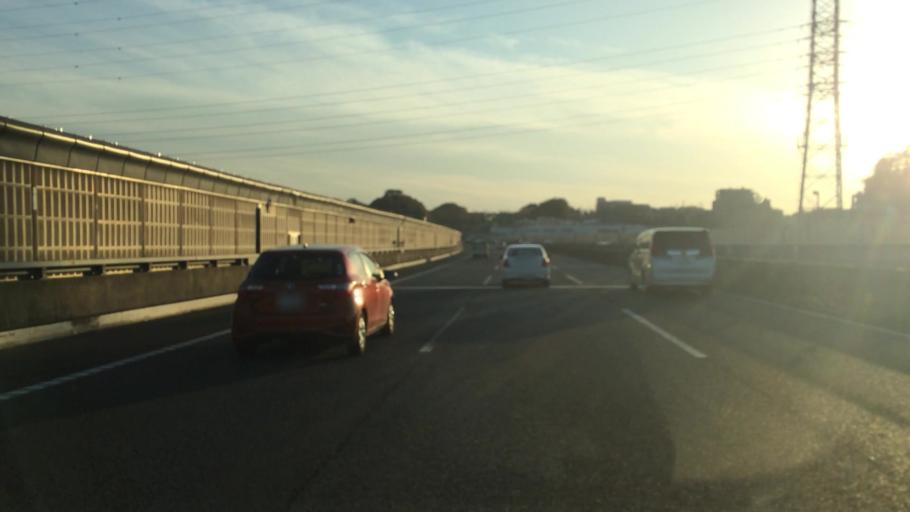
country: JP
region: Tokyo
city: Chofugaoka
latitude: 35.5869
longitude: 139.6210
